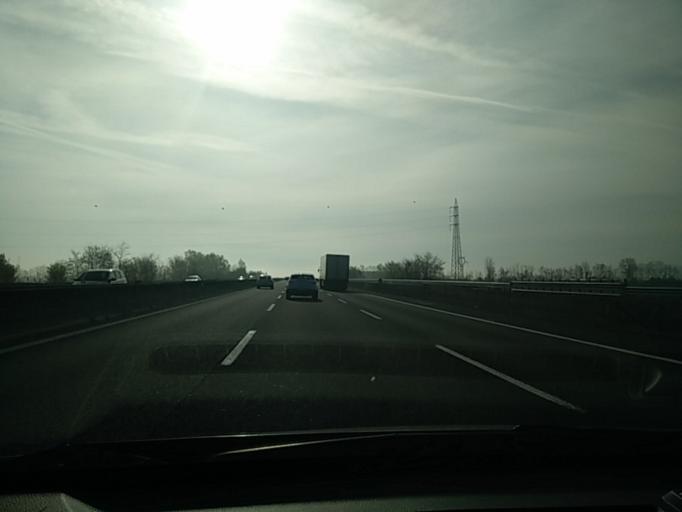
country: IT
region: Emilia-Romagna
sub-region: Provincia di Bologna
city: Ozzano dell'Emilia
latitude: 44.4655
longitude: 11.4878
